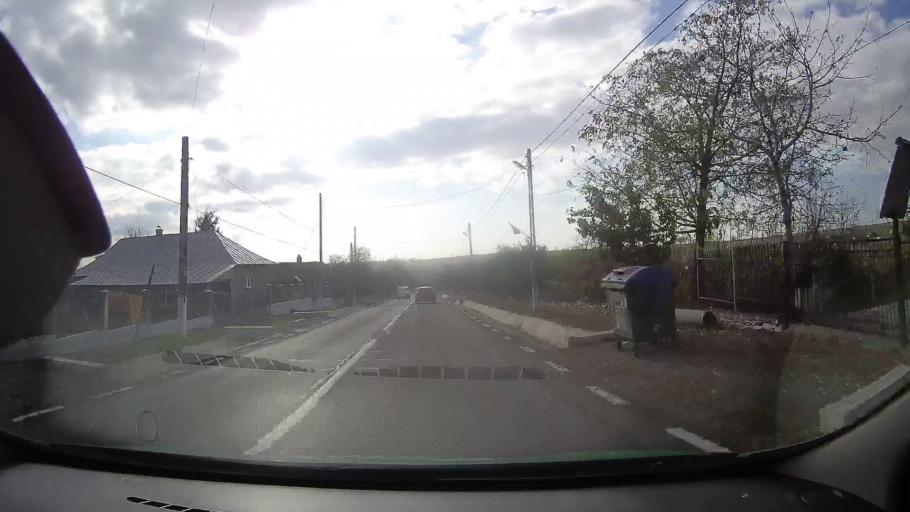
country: RO
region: Tulcea
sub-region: Comuna Topolog
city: Topolog
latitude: 44.8850
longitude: 28.3829
